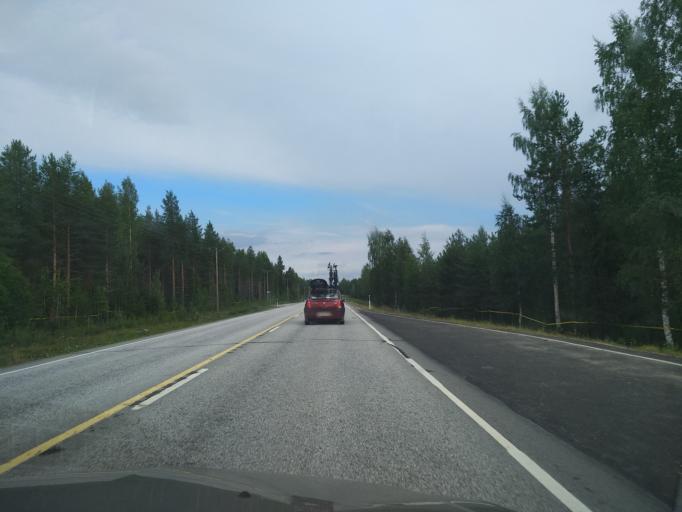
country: FI
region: Kainuu
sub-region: Kajaani
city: Paltamo
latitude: 64.3976
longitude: 27.9124
